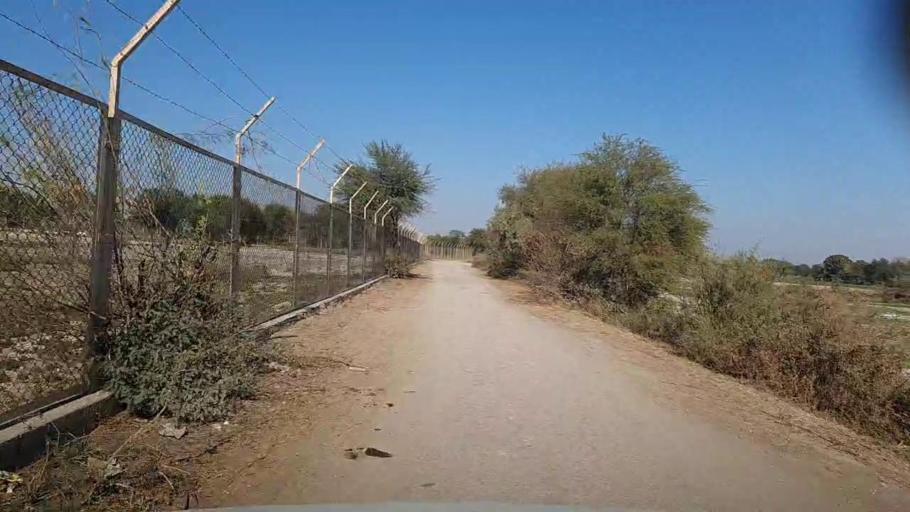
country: PK
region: Sindh
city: Khairpur
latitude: 27.9280
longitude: 69.7311
